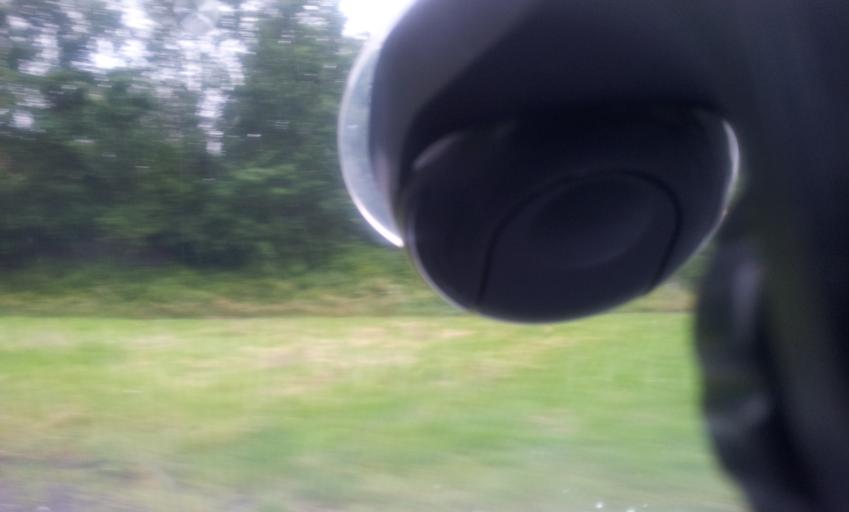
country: SE
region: OEstergoetland
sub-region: Norrkopings Kommun
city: Norrkoping
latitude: 58.5758
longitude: 16.1797
